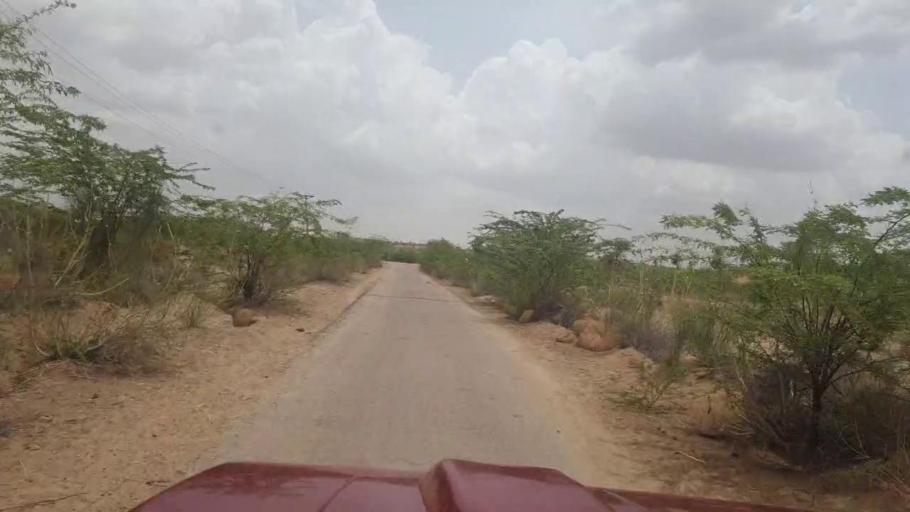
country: PK
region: Sindh
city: Islamkot
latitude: 25.1029
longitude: 70.3709
